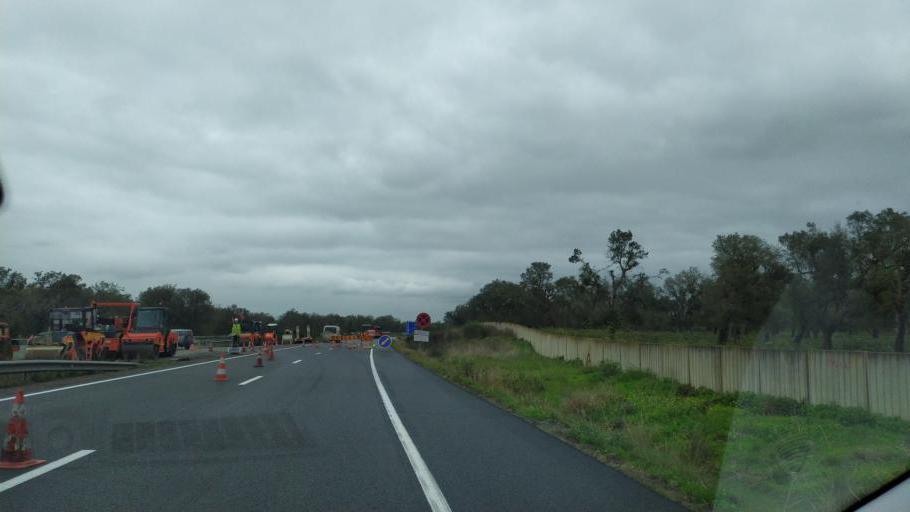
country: MA
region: Gharb-Chrarda-Beni Hssen
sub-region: Kenitra Province
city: Kenitra
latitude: 34.2246
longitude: -6.6013
